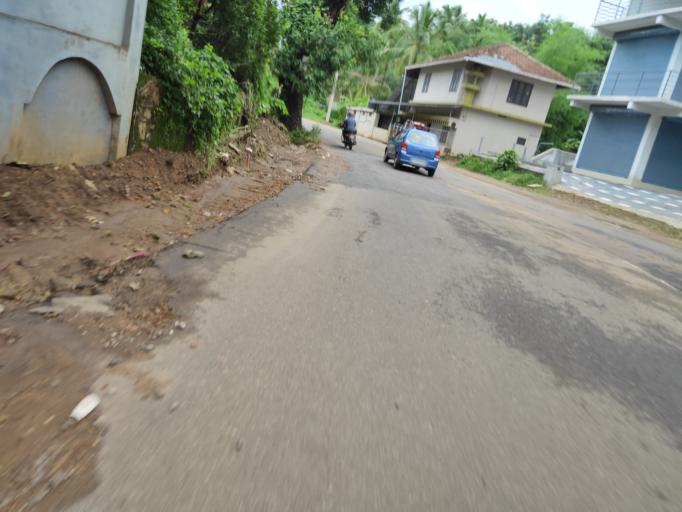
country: IN
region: Kerala
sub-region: Malappuram
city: Manjeri
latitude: 11.1920
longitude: 76.2510
